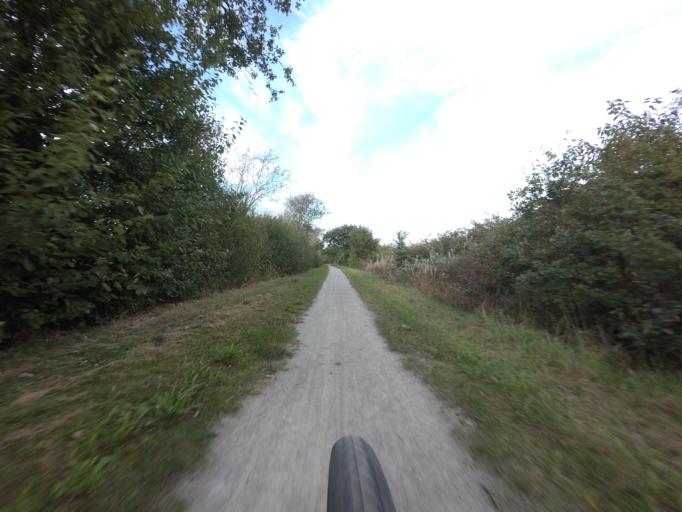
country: DK
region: Central Jutland
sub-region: Ikast-Brande Kommune
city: Brande
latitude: 55.9253
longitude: 9.1388
